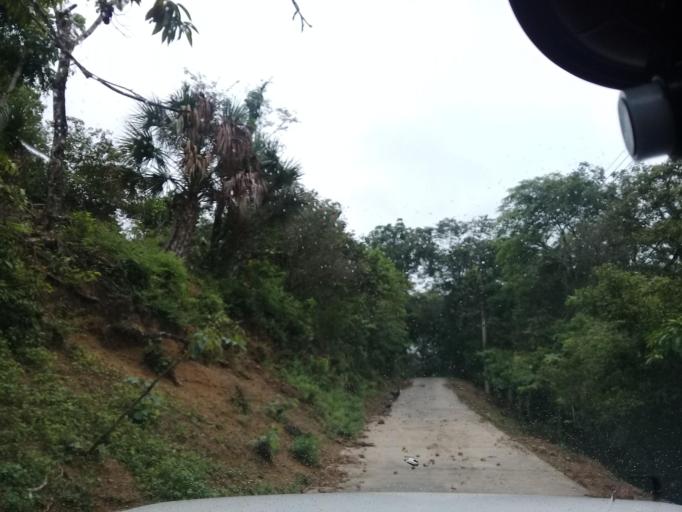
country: MX
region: Veracruz
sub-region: Chalma
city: San Pedro Coyutla
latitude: 21.2401
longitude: -98.4272
